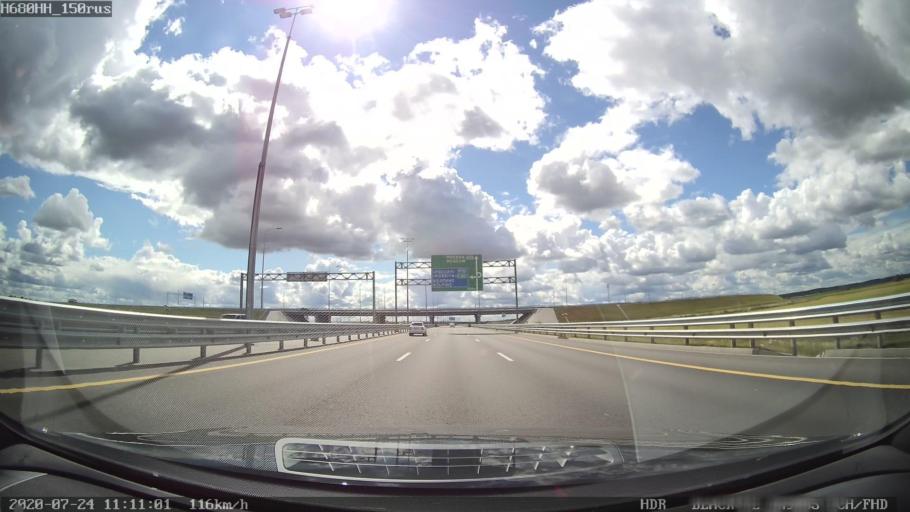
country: RU
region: St.-Petersburg
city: Tyarlevo
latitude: 59.7292
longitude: 30.5104
